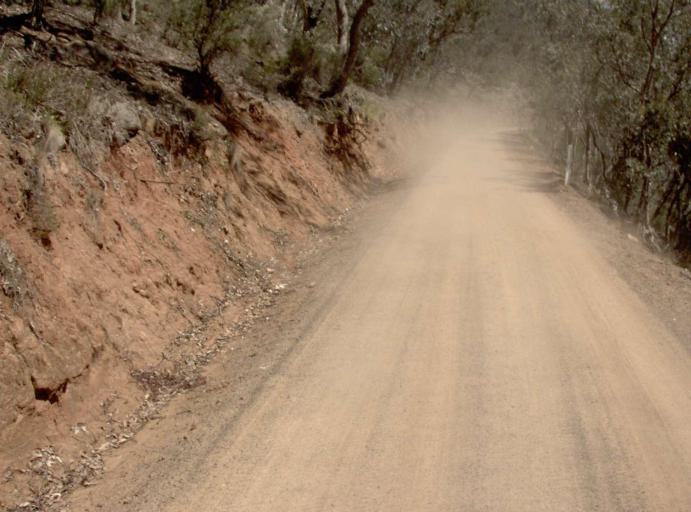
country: AU
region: New South Wales
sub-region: Snowy River
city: Jindabyne
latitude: -37.0482
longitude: 148.5393
